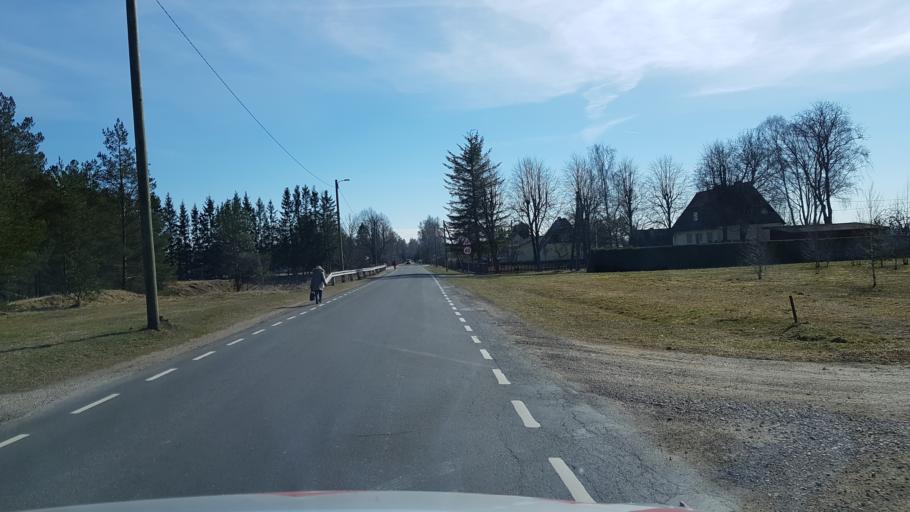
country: EE
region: Harju
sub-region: Nissi vald
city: Riisipere
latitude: 59.1100
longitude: 24.3142
